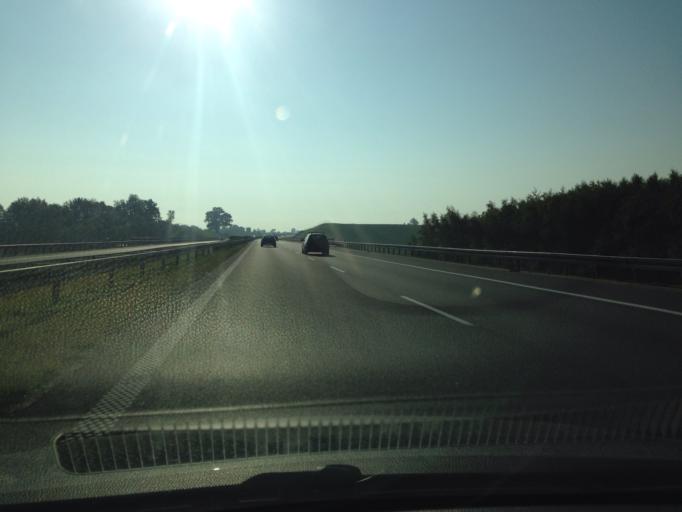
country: PL
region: Pomeranian Voivodeship
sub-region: Powiat gdanski
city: Legowo
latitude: 54.1834
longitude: 18.6407
